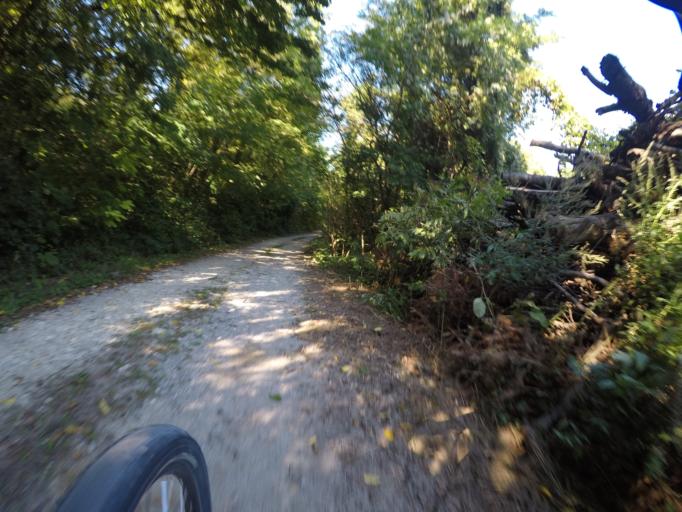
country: AT
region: Lower Austria
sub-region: Politischer Bezirk Bruck an der Leitha
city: Mannersdorf am Leithagebirge
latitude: 47.9564
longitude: 16.6073
